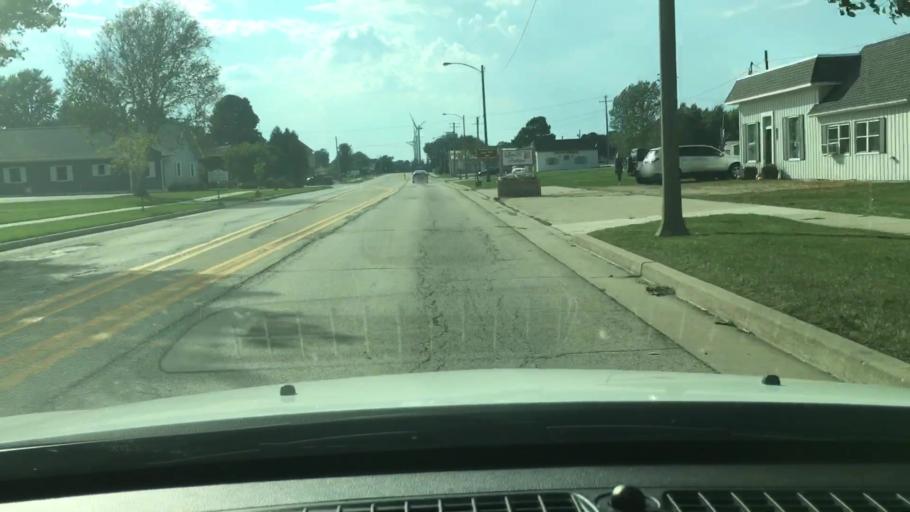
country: US
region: Illinois
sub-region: DeKalb County
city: Waterman
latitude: 41.7680
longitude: -88.8754
